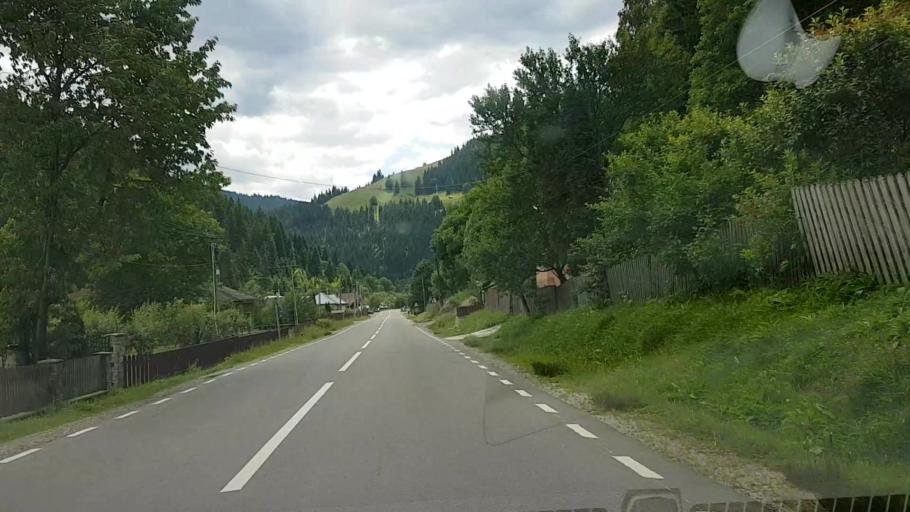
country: RO
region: Neamt
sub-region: Comuna Farcasa
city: Farcasa
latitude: 47.1483
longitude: 25.8647
